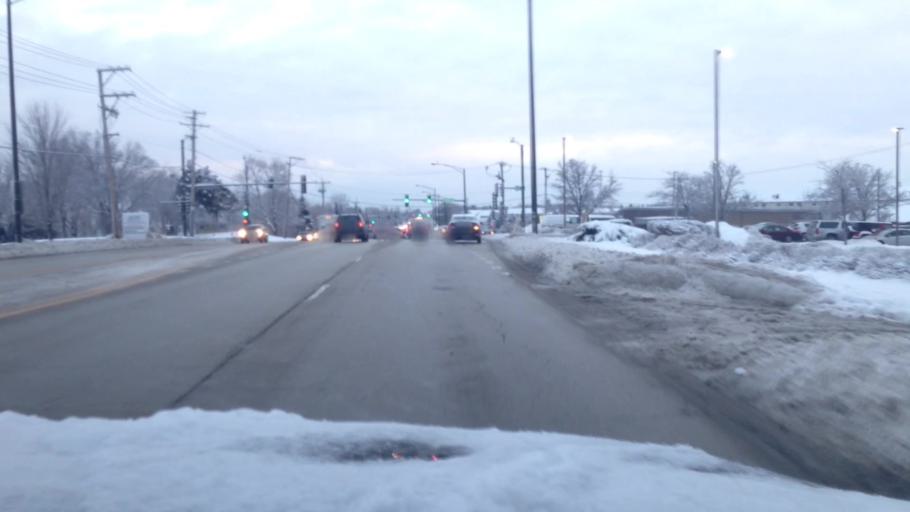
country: US
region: Illinois
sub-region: Kane County
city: South Elgin
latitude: 42.0081
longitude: -88.3151
